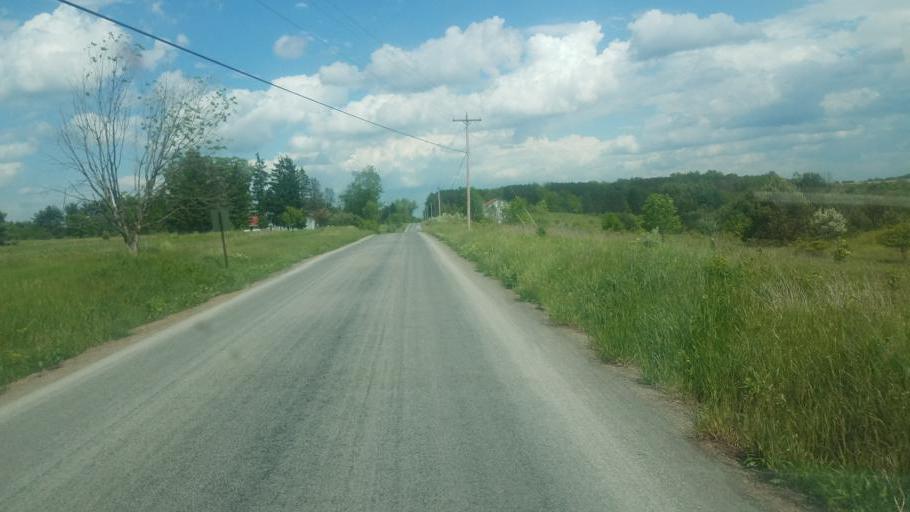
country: US
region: Pennsylvania
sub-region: Venango County
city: Franklin
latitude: 41.2272
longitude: -79.8395
